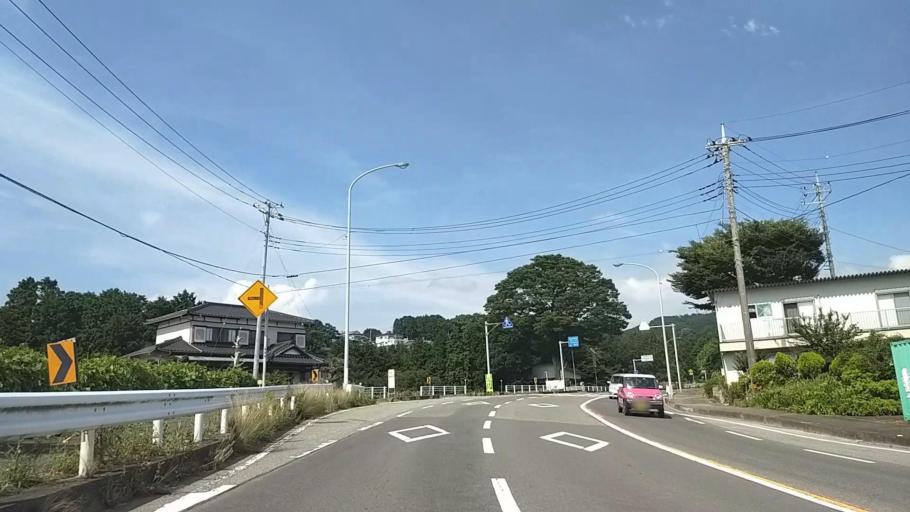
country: JP
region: Shizuoka
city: Mishima
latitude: 35.1433
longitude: 138.9773
